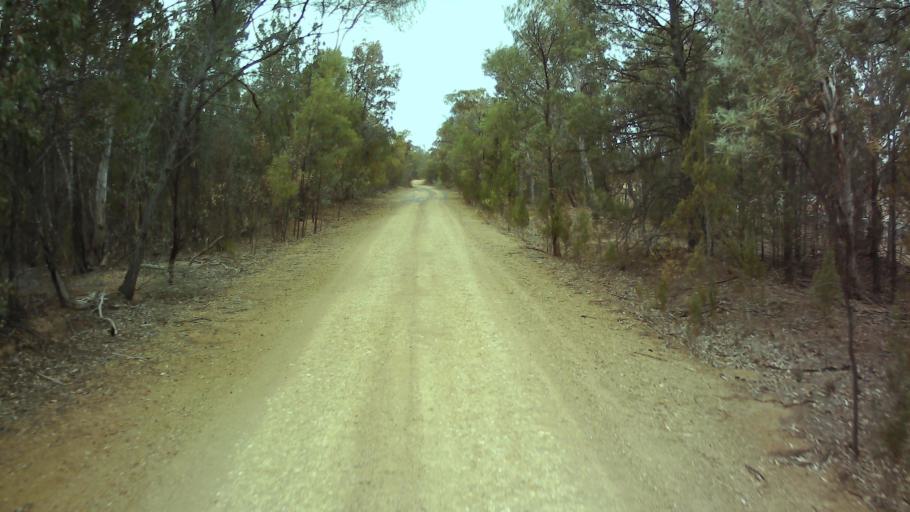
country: AU
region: New South Wales
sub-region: Weddin
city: Grenfell
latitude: -33.8874
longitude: 148.1572
